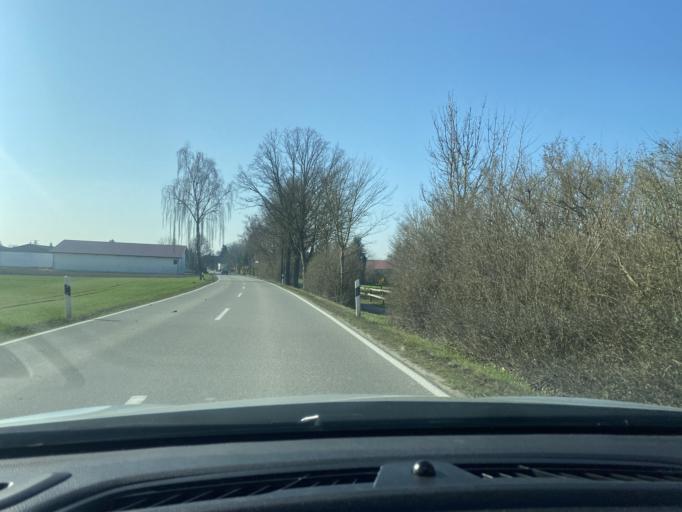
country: DE
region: Bavaria
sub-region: Upper Bavaria
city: Oberding
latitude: 48.3092
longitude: 11.8474
